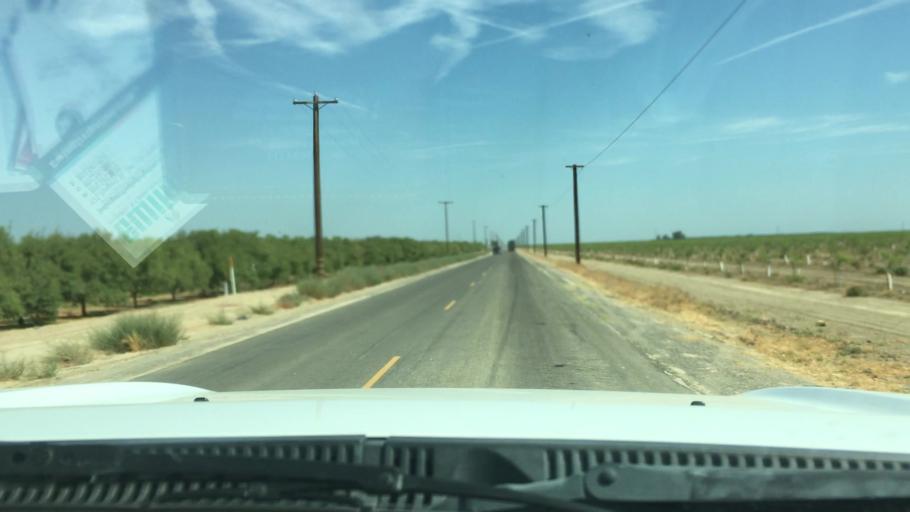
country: US
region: California
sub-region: Kern County
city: Shafter
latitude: 35.4498
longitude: -119.3681
